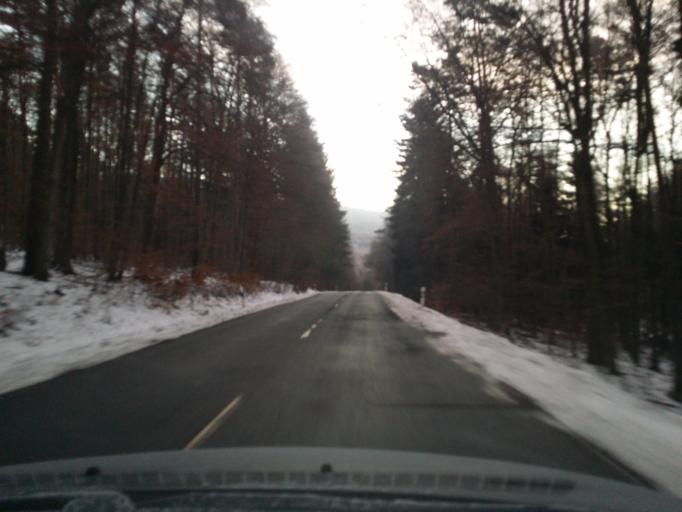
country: DE
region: Hesse
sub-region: Regierungsbezirk Darmstadt
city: Glashutten
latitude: 50.1874
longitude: 8.3572
